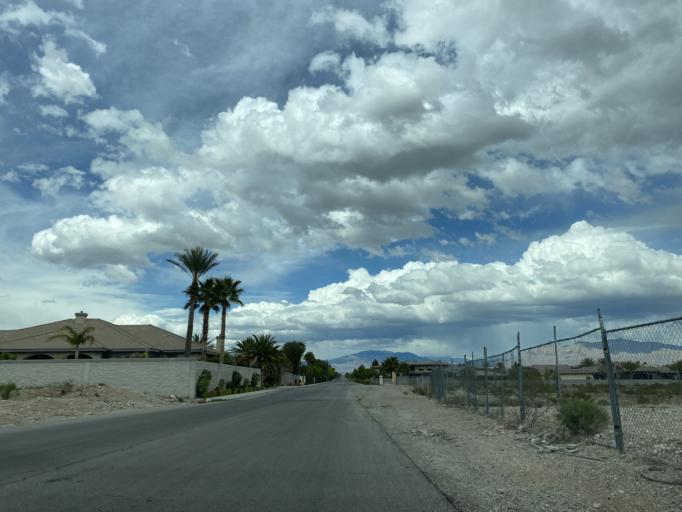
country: US
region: Nevada
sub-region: Clark County
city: Summerlin South
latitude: 36.2415
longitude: -115.2837
